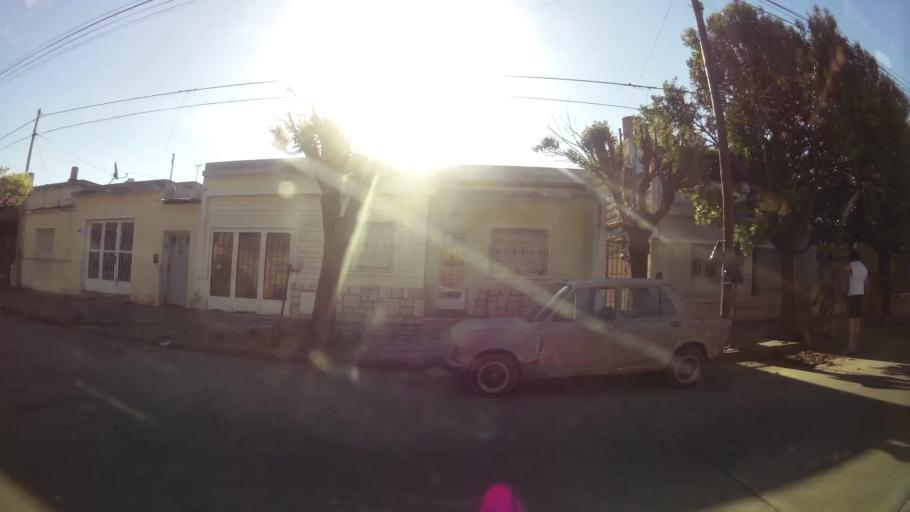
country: AR
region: Cordoba
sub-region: Departamento de Capital
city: Cordoba
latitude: -31.3822
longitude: -64.1893
